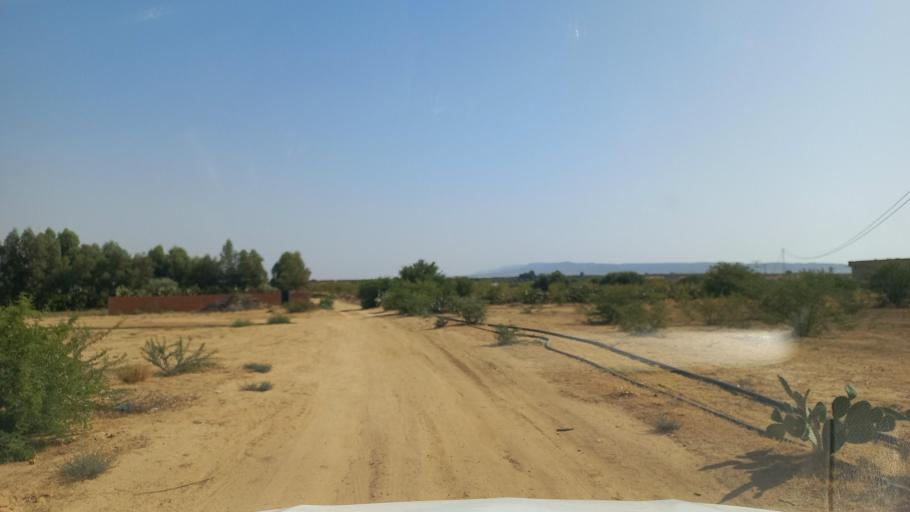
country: TN
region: Al Qasrayn
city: Kasserine
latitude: 35.2446
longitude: 9.0421
